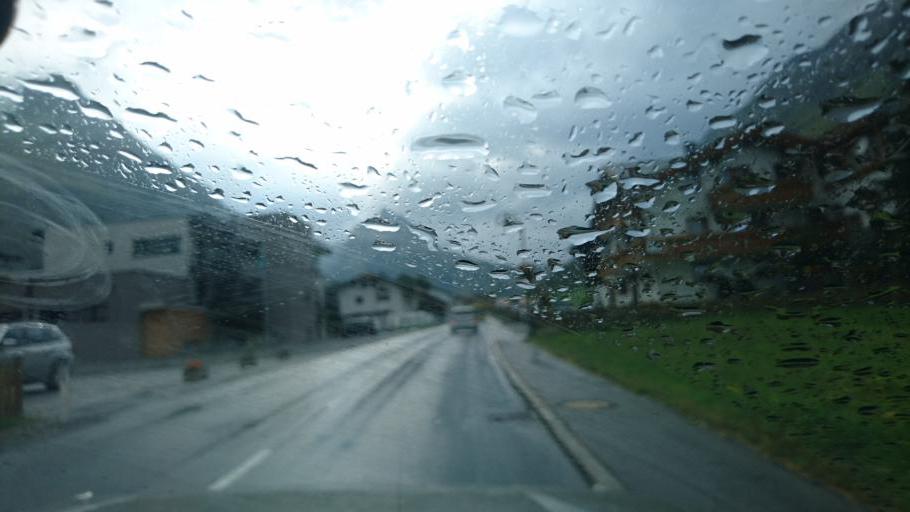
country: AT
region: Tyrol
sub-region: Politischer Bezirk Landeck
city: Galtur
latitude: 46.9710
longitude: 10.1958
